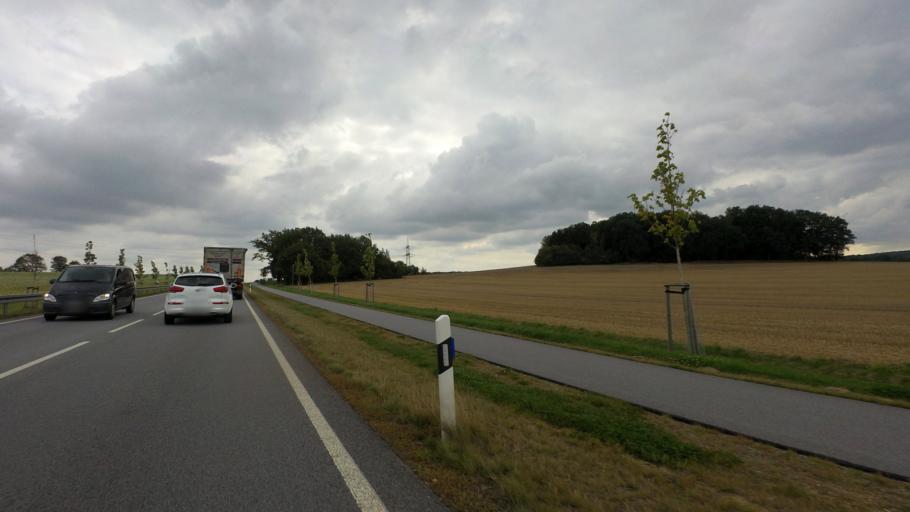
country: DE
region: Saxony
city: Radibor
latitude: 51.2441
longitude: 14.3619
